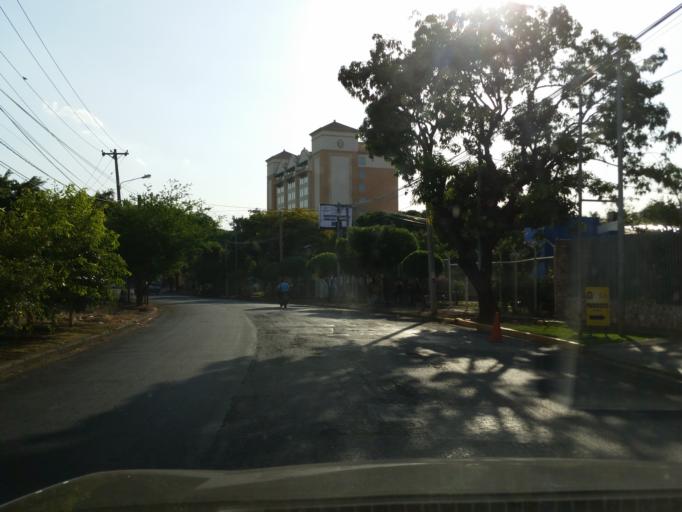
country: NI
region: Managua
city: Managua
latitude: 12.1266
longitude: -86.2630
